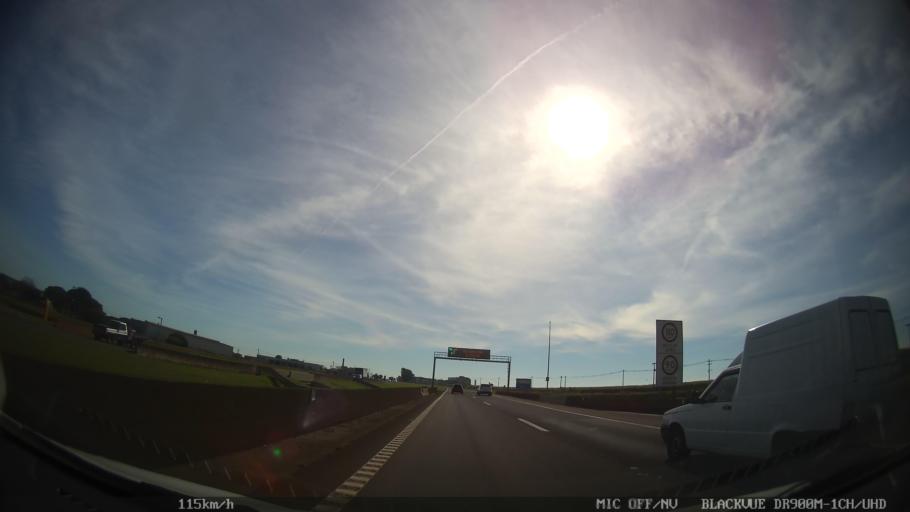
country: BR
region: Sao Paulo
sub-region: Araras
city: Araras
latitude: -22.4174
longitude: -47.3905
